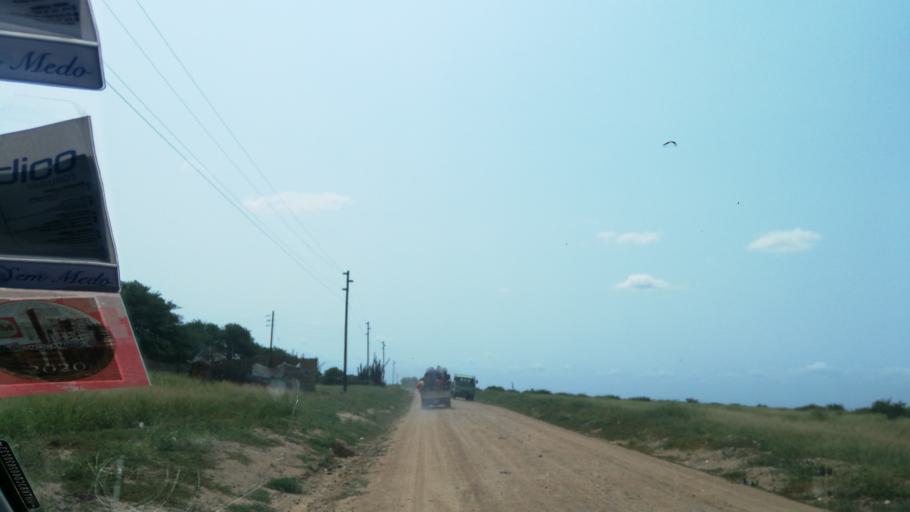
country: MZ
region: Maputo
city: Matola
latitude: -26.0648
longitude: 32.3901
